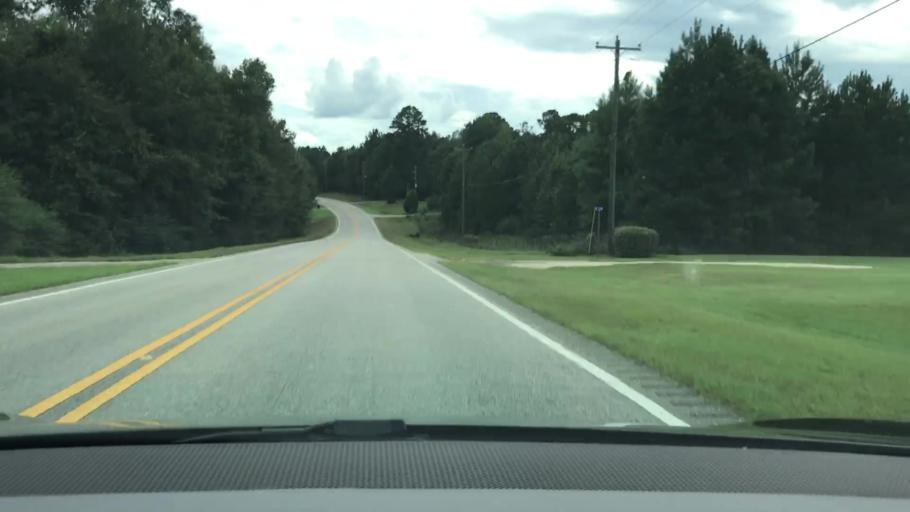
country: US
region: Alabama
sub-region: Pike County
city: Troy
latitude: 31.6541
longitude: -85.9665
